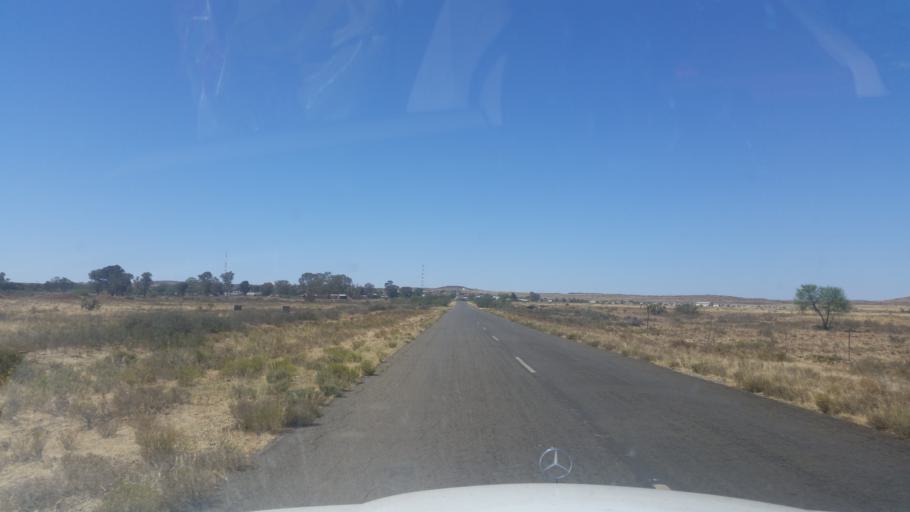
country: ZA
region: Eastern Cape
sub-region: Joe Gqabi District Municipality
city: Burgersdorp
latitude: -30.7687
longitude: 25.7900
